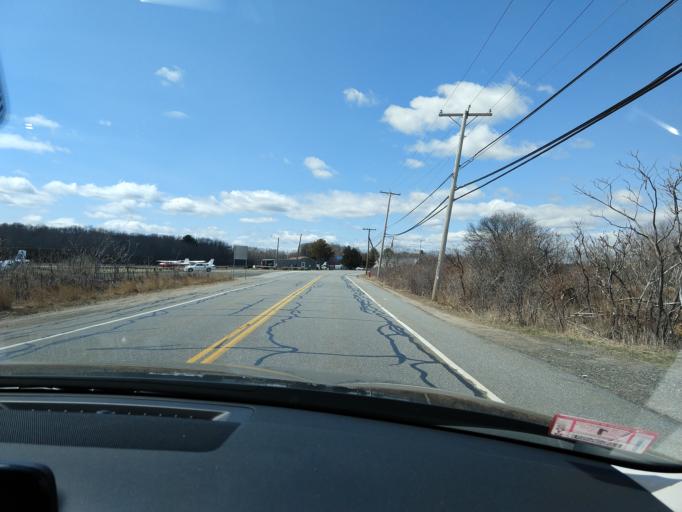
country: US
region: Massachusetts
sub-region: Essex County
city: Newburyport
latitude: 42.7960
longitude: -70.8397
